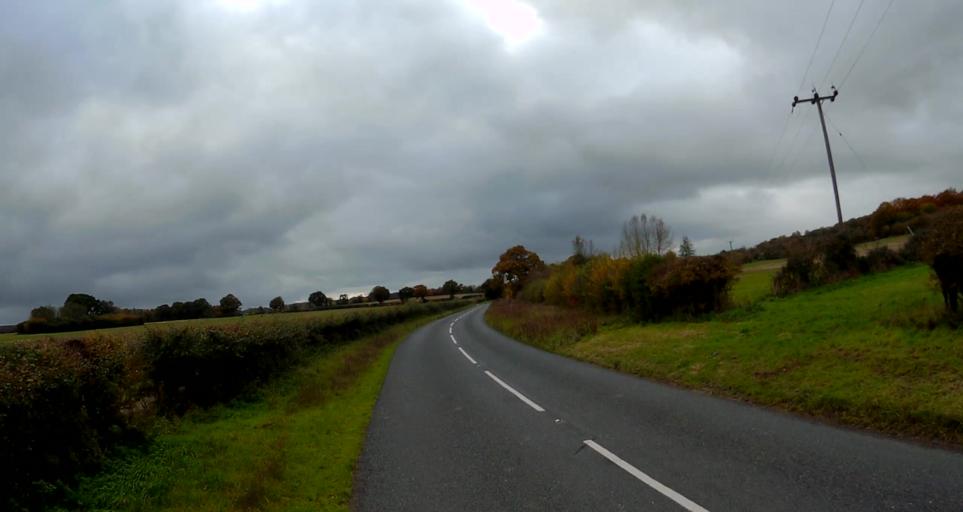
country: GB
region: England
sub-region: Hampshire
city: Four Marks
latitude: 51.1621
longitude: -1.1435
